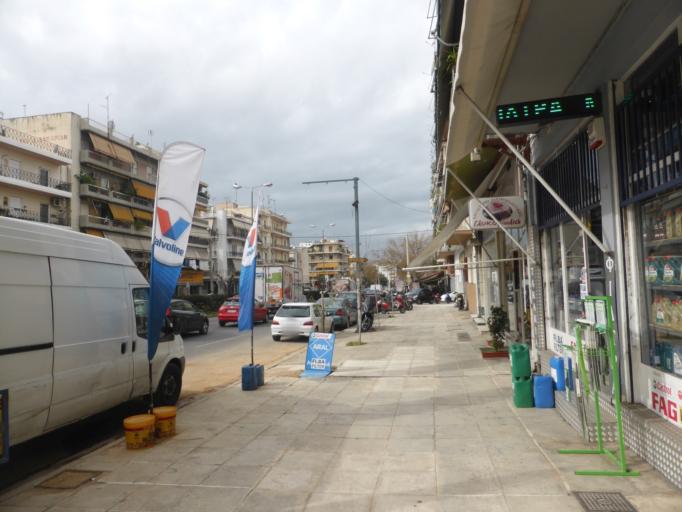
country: GR
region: Attica
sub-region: Nomarchia Athinas
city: Tavros
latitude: 37.9673
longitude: 23.7048
